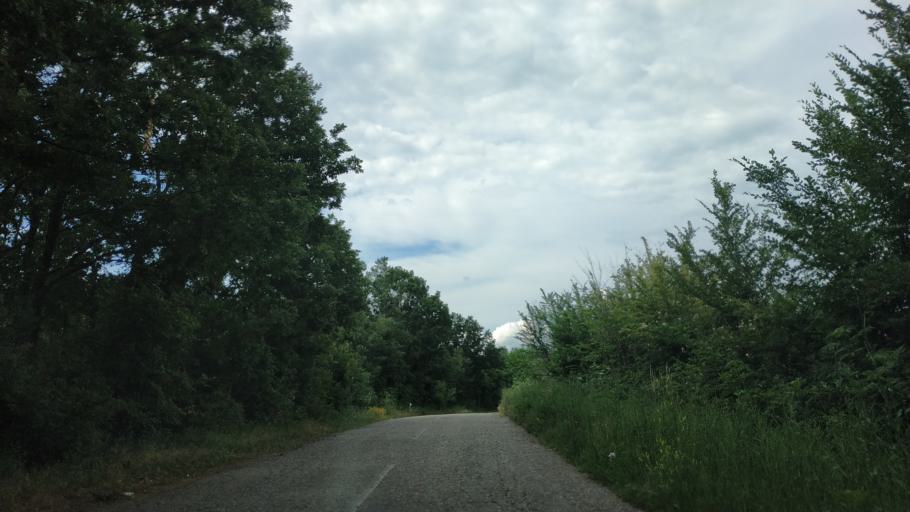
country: RS
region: Central Serbia
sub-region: Nisavski Okrug
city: Aleksinac
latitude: 43.6072
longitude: 21.6475
